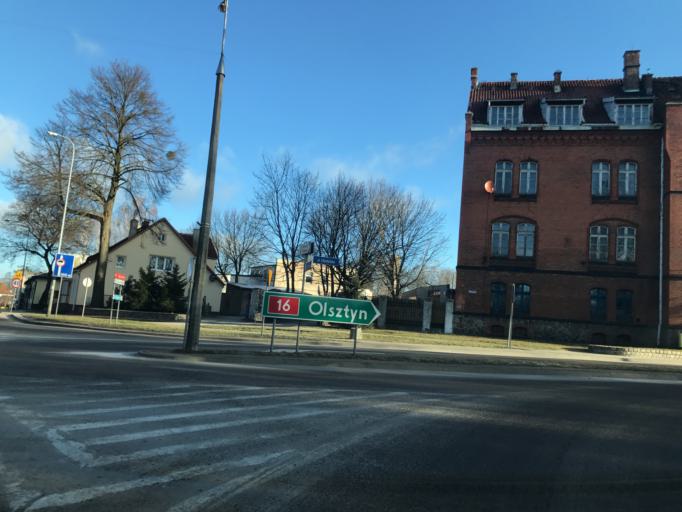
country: PL
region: Warmian-Masurian Voivodeship
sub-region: Powiat ostrodzki
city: Ostroda
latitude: 53.7051
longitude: 19.9598
